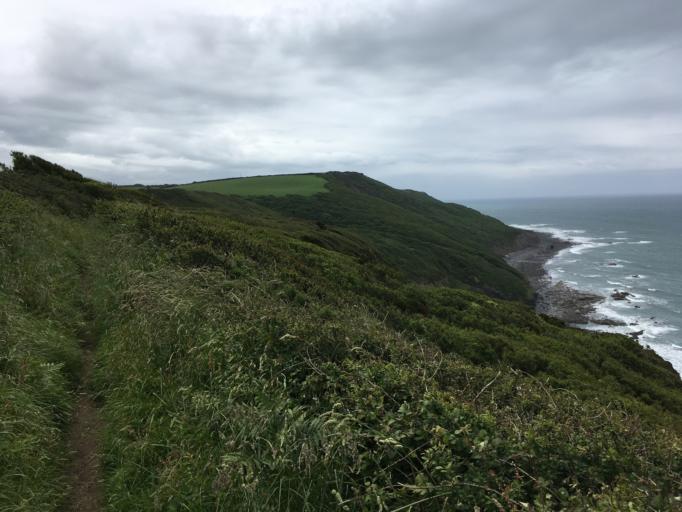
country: GB
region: England
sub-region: Cornwall
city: Poundstock
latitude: 50.7673
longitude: -4.5854
